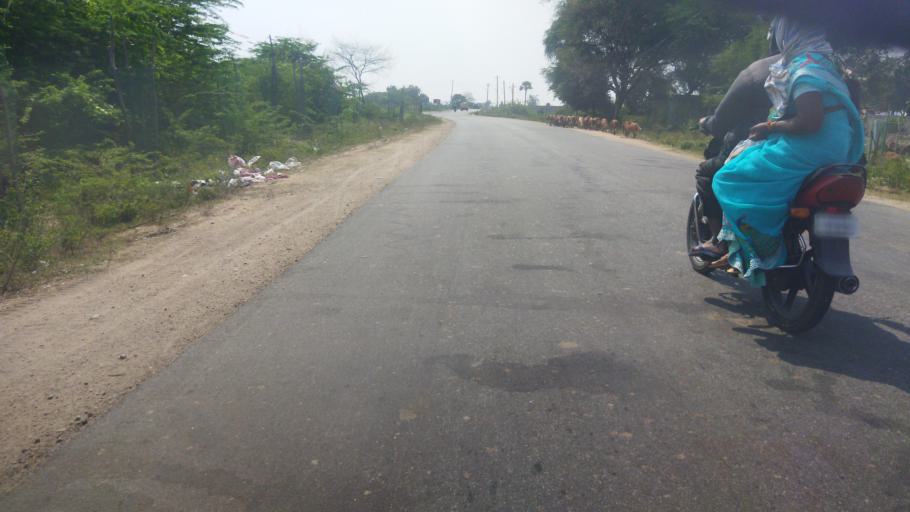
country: IN
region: Telangana
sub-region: Nalgonda
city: Nalgonda
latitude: 17.0853
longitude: 79.2845
